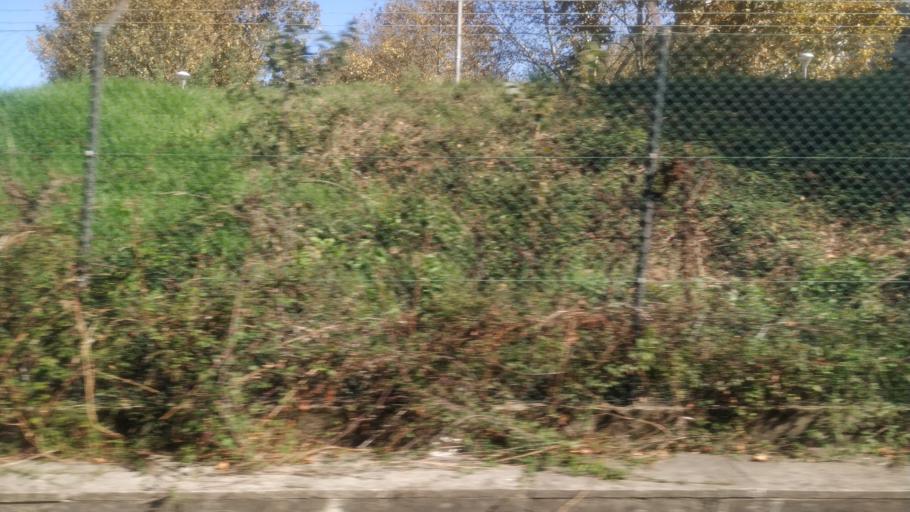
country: PT
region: Porto
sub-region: Matosinhos
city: Senhora da Hora
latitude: 41.1830
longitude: -8.6645
